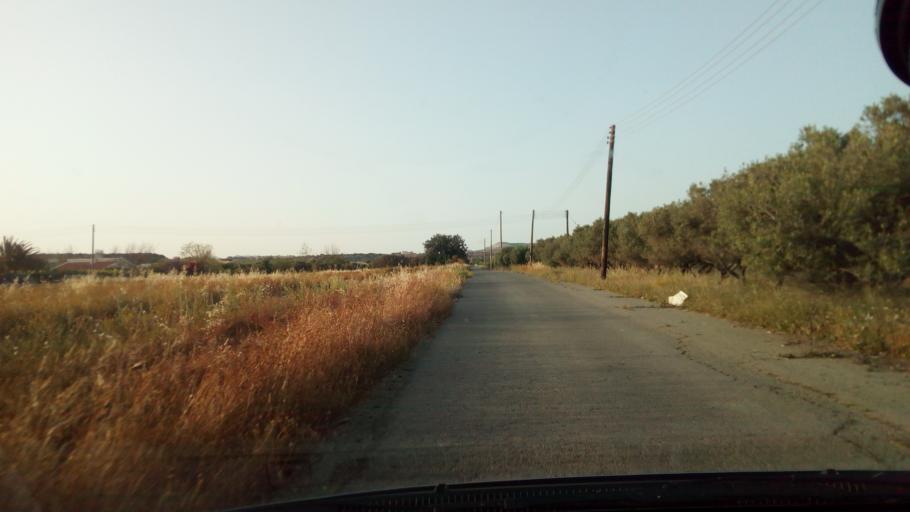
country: CY
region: Larnaka
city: Kofinou
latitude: 34.7369
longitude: 33.3505
